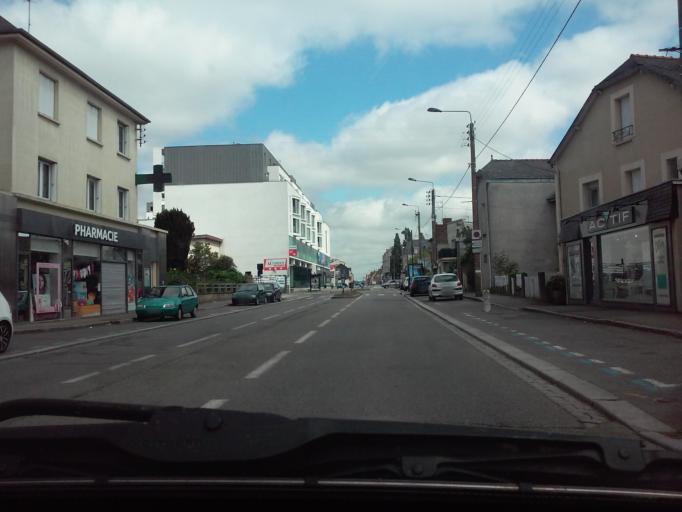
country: FR
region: Brittany
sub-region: Departement d'Ille-et-Vilaine
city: Rennes
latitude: 48.0915
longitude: -1.6921
